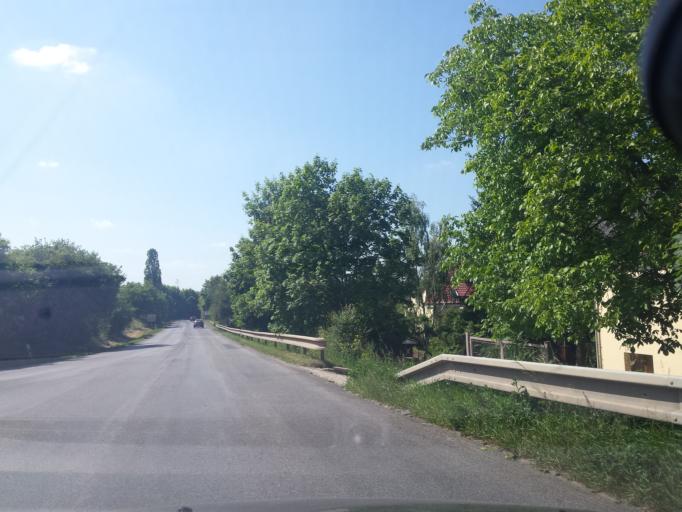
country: CZ
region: Central Bohemia
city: Horomerice
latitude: 50.1450
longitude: 14.3342
